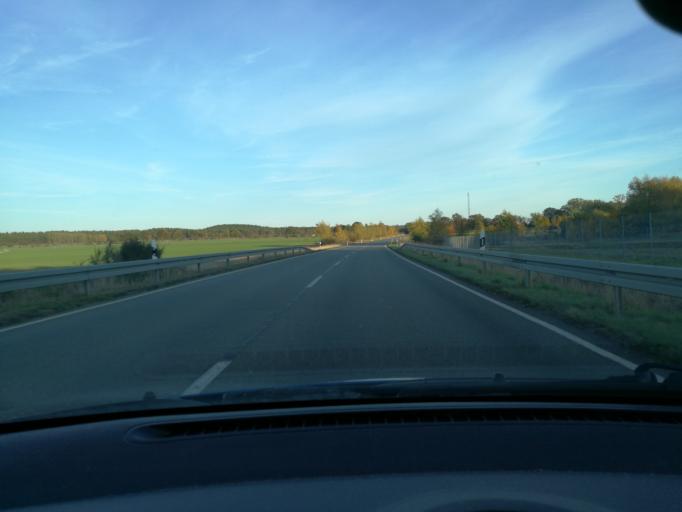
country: DE
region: Brandenburg
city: Perleberg
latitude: 53.0894
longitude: 11.8916
